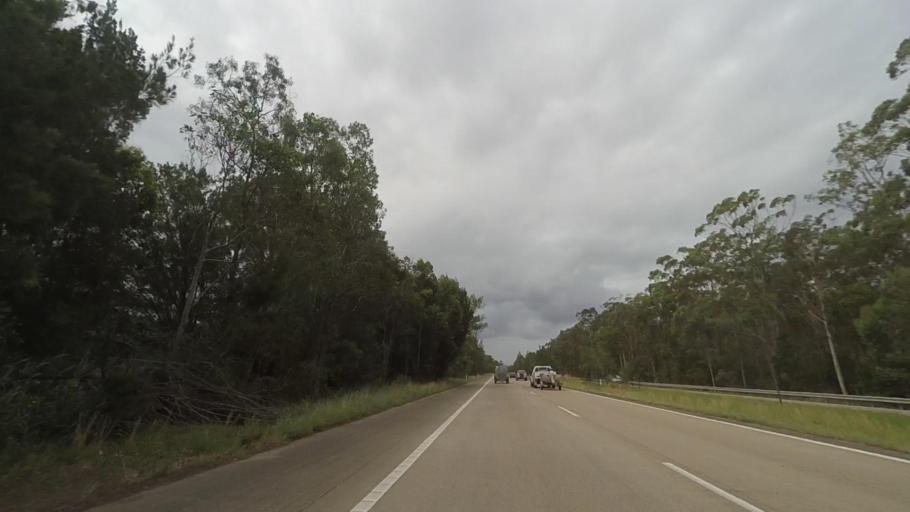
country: AU
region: New South Wales
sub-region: Port Stephens Shire
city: Raymond Terrace
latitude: -32.7238
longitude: 151.7871
